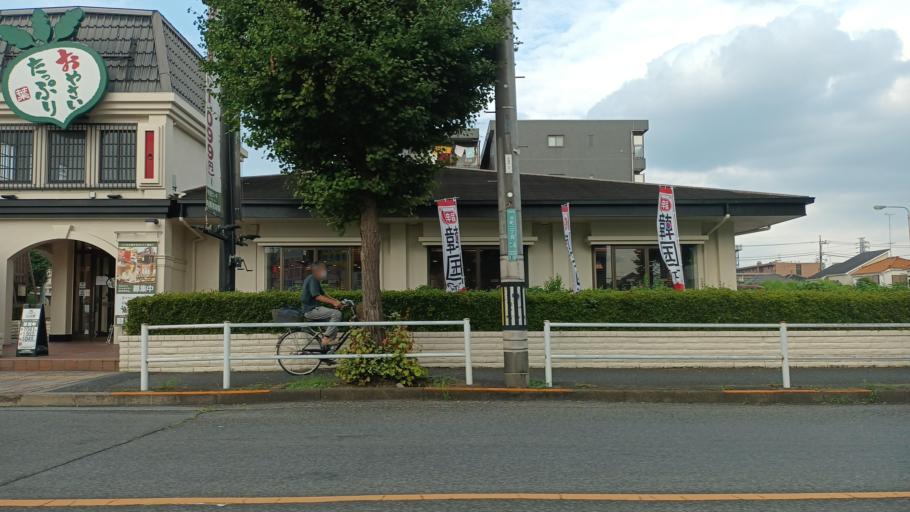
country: JP
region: Tokyo
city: Fussa
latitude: 35.7706
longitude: 139.3093
